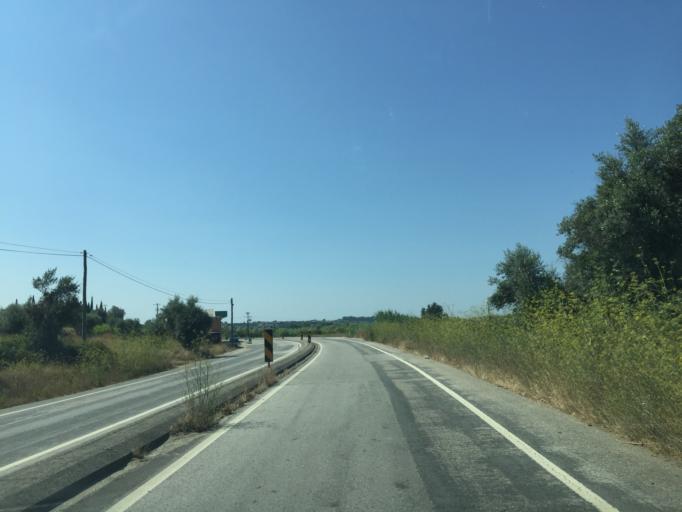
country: PT
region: Aveiro
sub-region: Mealhada
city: Mealhada
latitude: 40.3683
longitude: -8.4597
